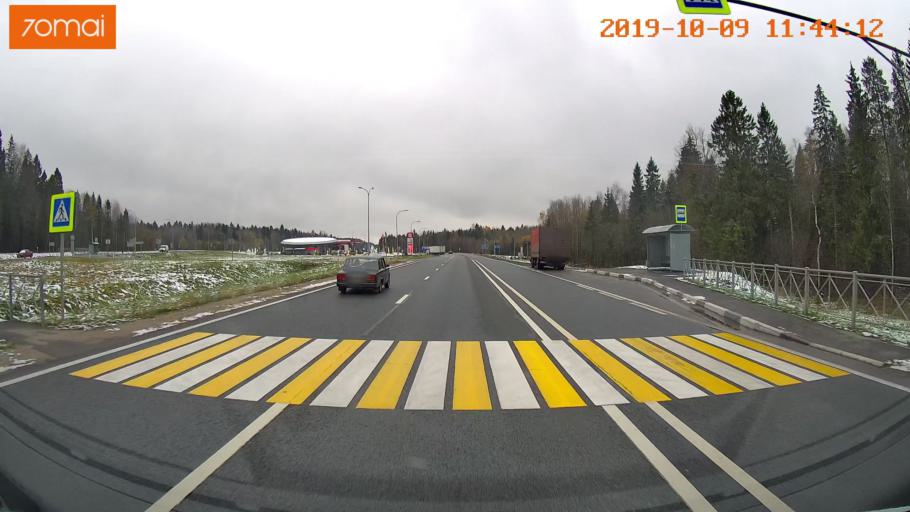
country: RU
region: Vologda
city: Gryazovets
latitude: 58.8863
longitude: 40.1900
